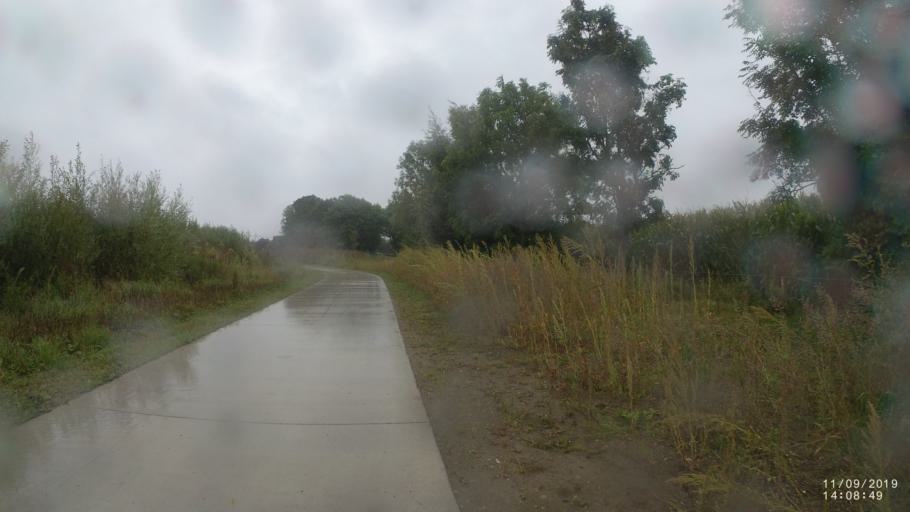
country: BE
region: Flanders
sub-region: Provincie Oost-Vlaanderen
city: Evergem
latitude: 51.0863
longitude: 3.6779
